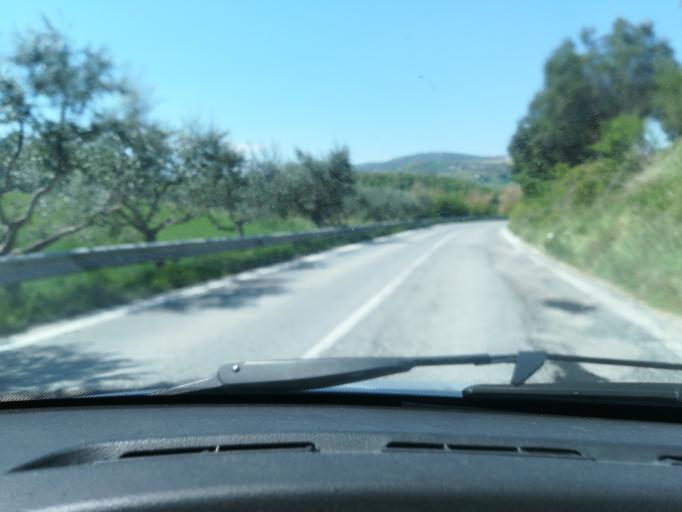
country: IT
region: The Marches
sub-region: Provincia di Macerata
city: Strada
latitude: 43.4001
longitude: 13.2052
